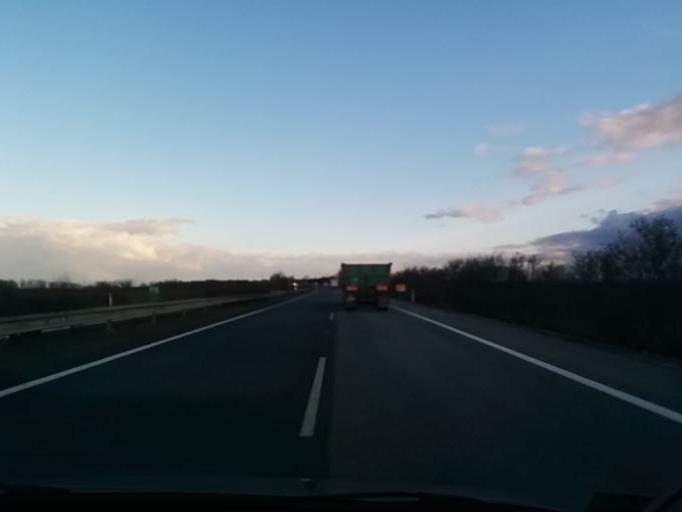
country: SK
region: Trnavsky
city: Leopoldov
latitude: 48.4137
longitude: 17.7478
